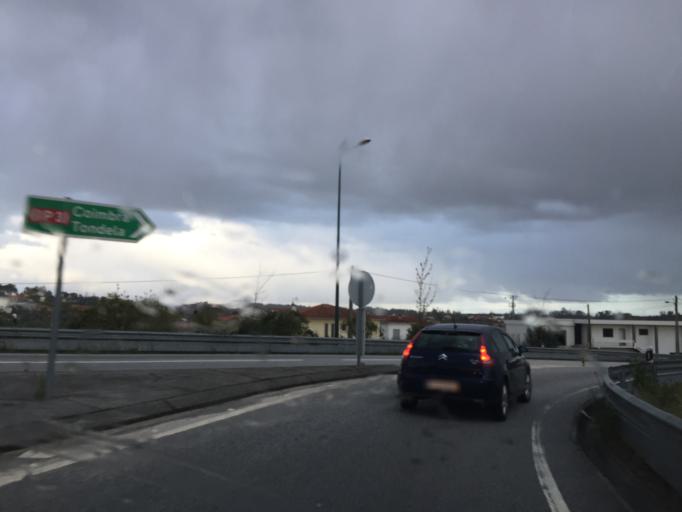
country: PT
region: Viseu
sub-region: Viseu
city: Viseu
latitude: 40.6161
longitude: -7.9561
